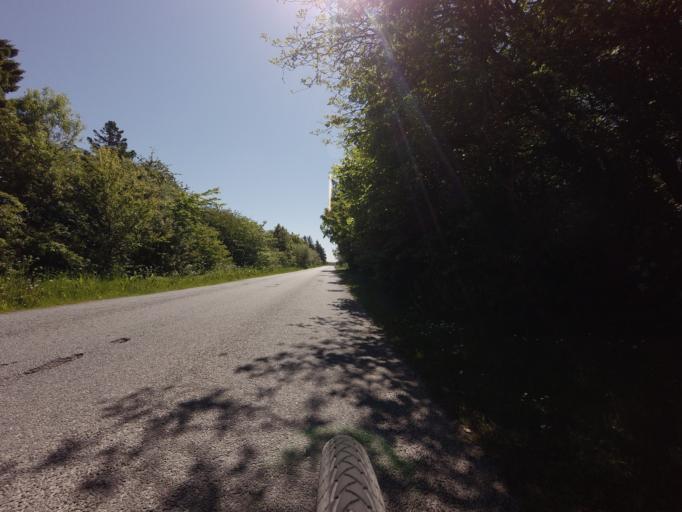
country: DK
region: North Denmark
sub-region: Hjorring Kommune
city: Vra
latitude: 57.4196
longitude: 9.7805
